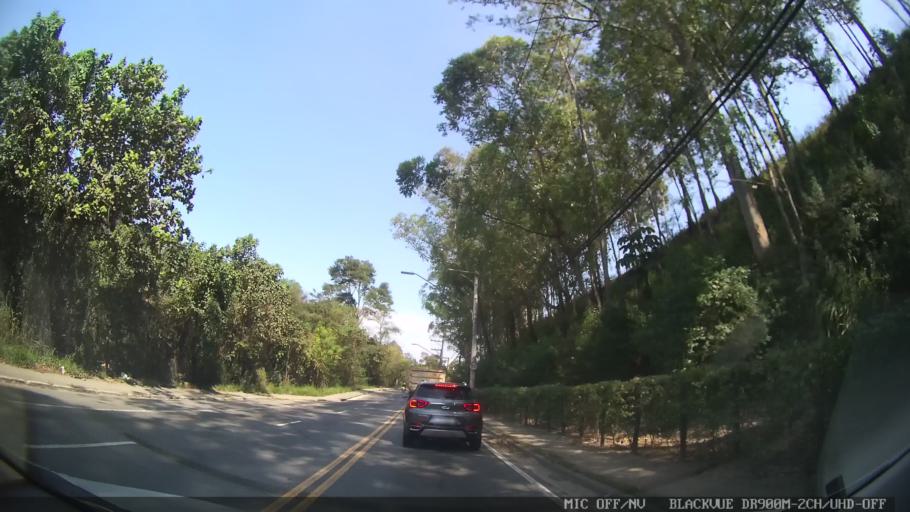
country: BR
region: Sao Paulo
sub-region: Caieiras
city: Caieiras
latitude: -23.4028
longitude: -46.7292
